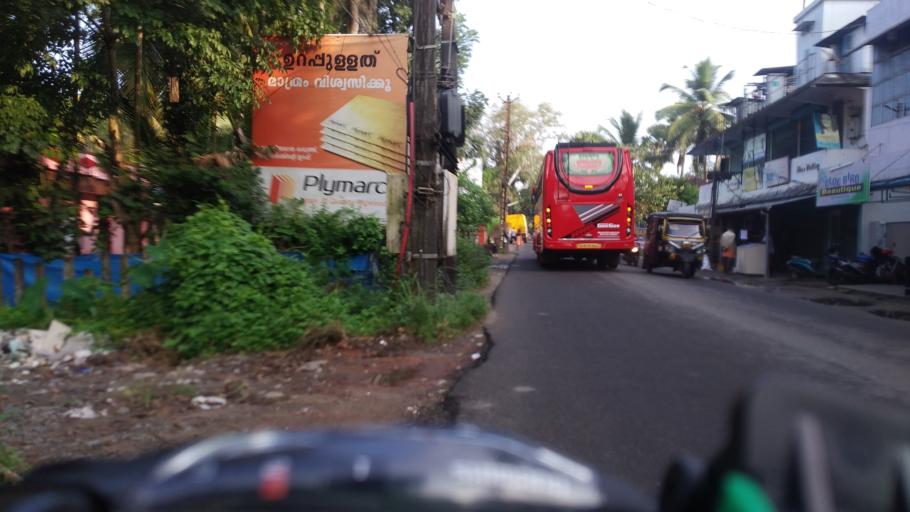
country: IN
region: Kerala
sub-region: Ernakulam
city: Elur
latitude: 10.0707
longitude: 76.2120
